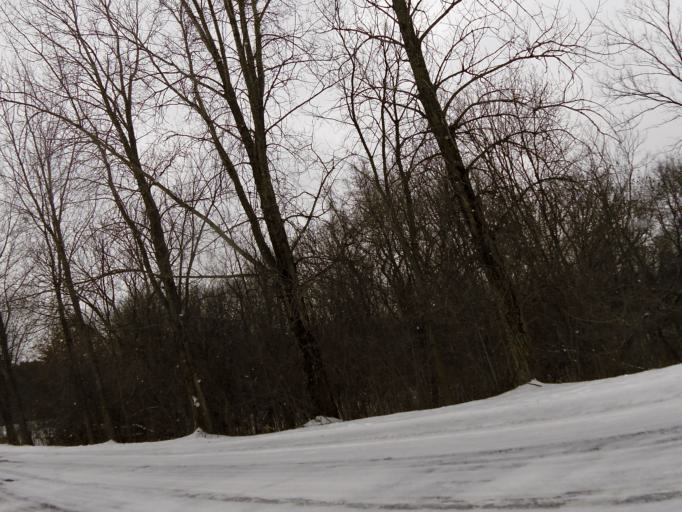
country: US
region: Minnesota
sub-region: Washington County
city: Lake Elmo
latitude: 44.9738
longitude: -92.8428
